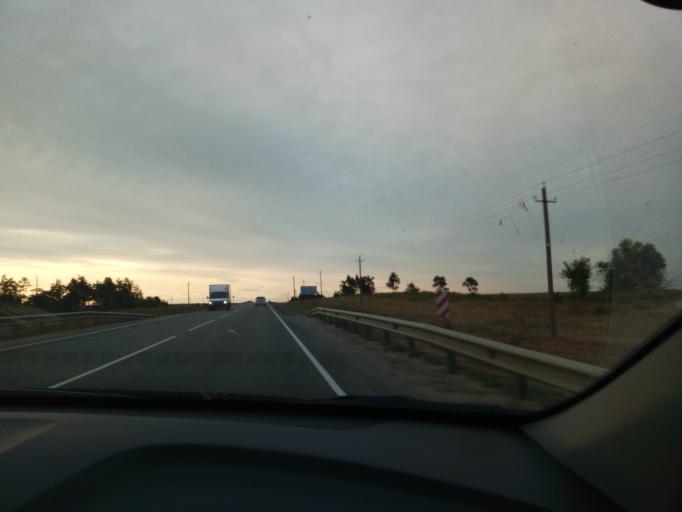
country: RU
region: Volgograd
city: Primorsk
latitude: 49.2507
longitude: 44.8888
